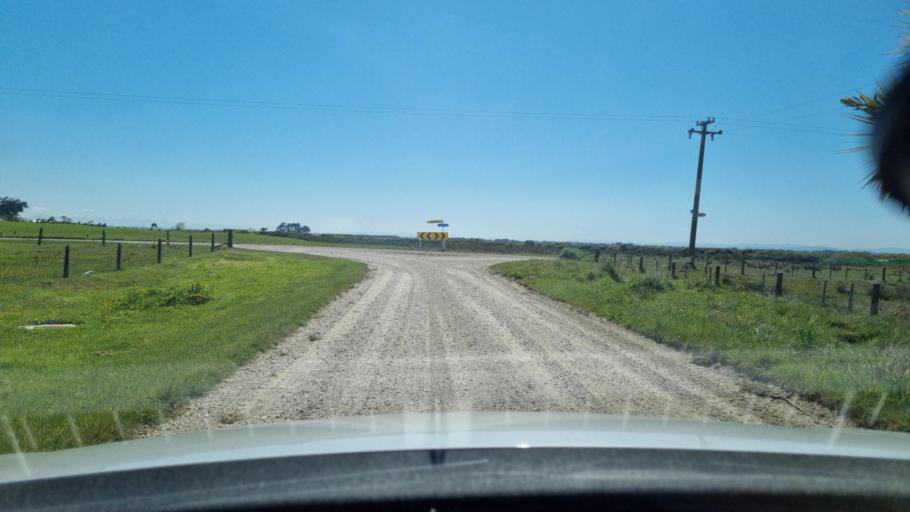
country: NZ
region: Southland
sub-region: Invercargill City
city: Invercargill
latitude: -46.4098
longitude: 168.2635
